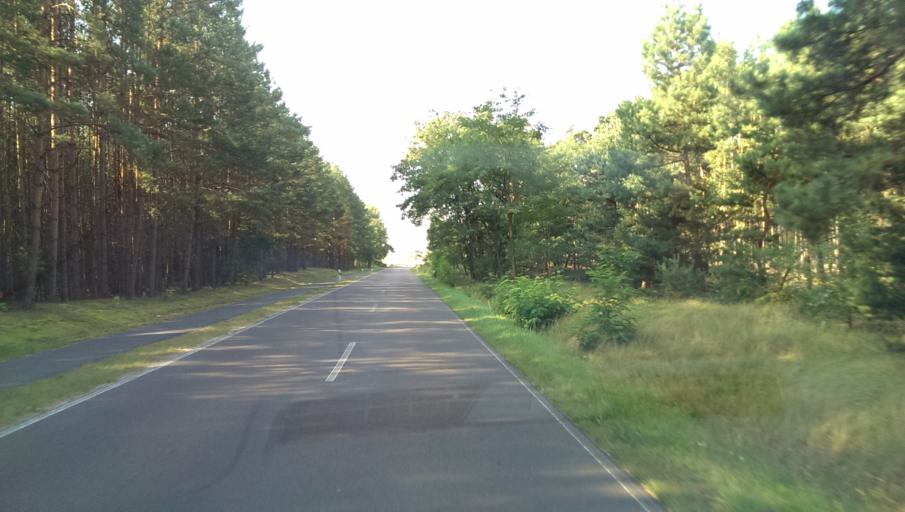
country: DE
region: Brandenburg
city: Luckenwalde
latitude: 52.1759
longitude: 13.1135
